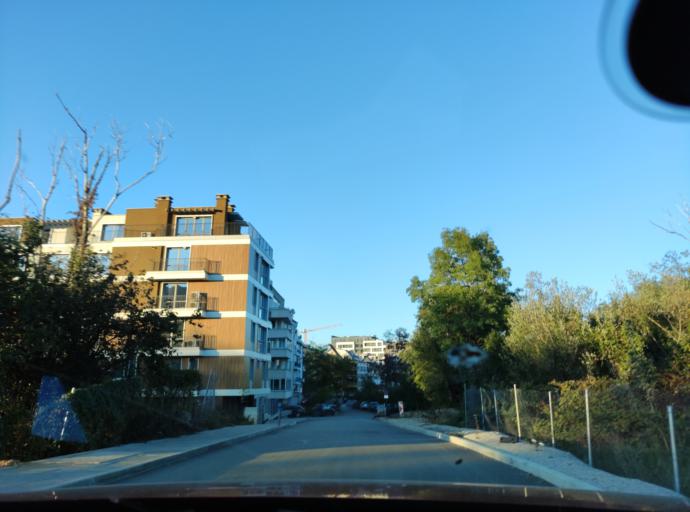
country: BG
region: Sofia-Capital
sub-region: Stolichna Obshtina
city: Sofia
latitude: 42.6591
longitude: 23.2931
